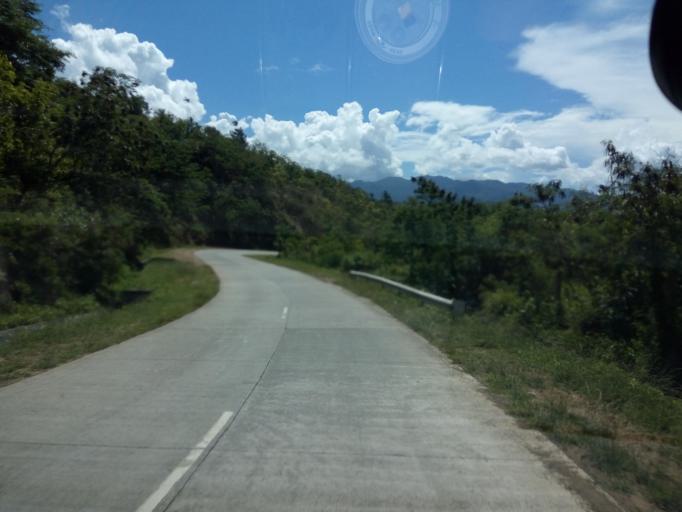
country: PH
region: Central Luzon
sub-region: Province of Nueva Ecija
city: General Luna
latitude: 15.7976
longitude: 121.2891
